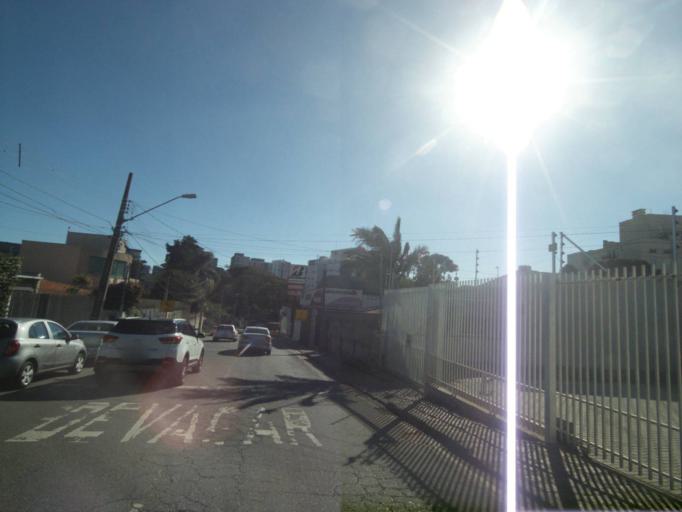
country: BR
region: Parana
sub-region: Curitiba
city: Curitiba
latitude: -25.4040
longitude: -49.2465
